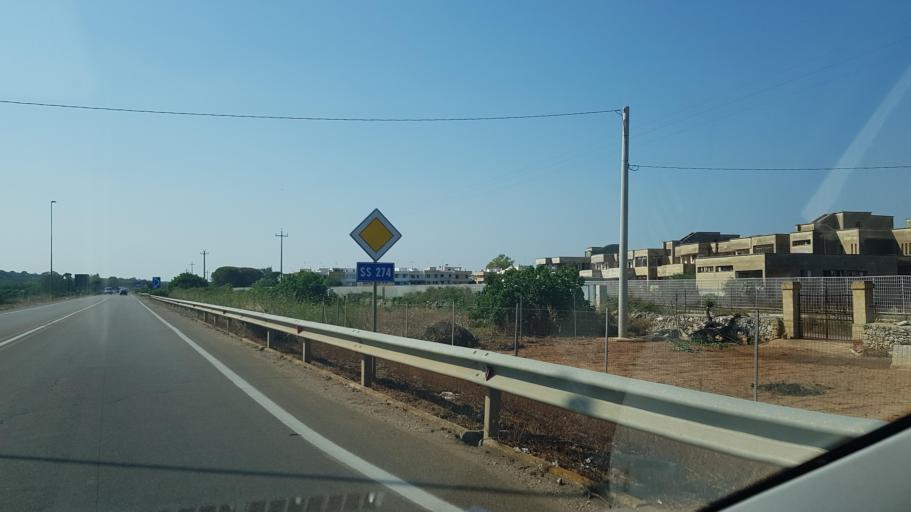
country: IT
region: Apulia
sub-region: Provincia di Lecce
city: Presicce
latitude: 39.8963
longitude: 18.2556
